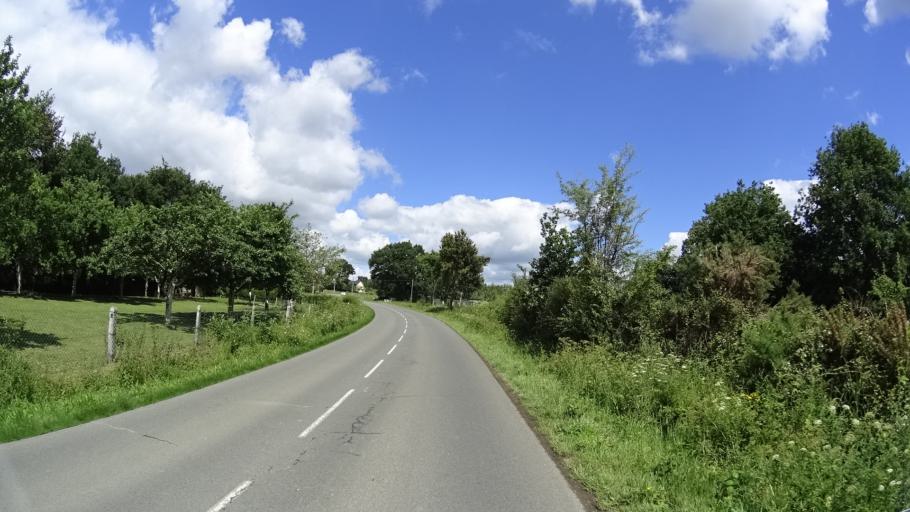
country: FR
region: Brittany
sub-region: Departement d'Ille-et-Vilaine
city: Saint-Gilles
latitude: 48.1365
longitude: -1.8258
